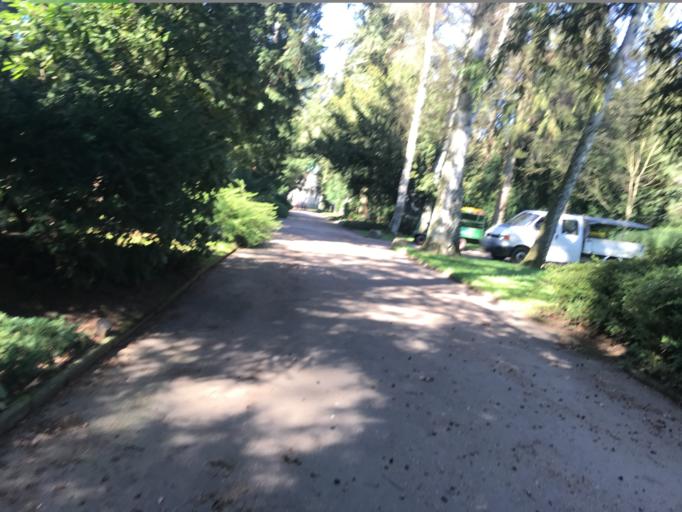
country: DE
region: Hesse
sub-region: Regierungsbezirk Darmstadt
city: Frankfurt am Main
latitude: 50.1361
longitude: 8.6884
